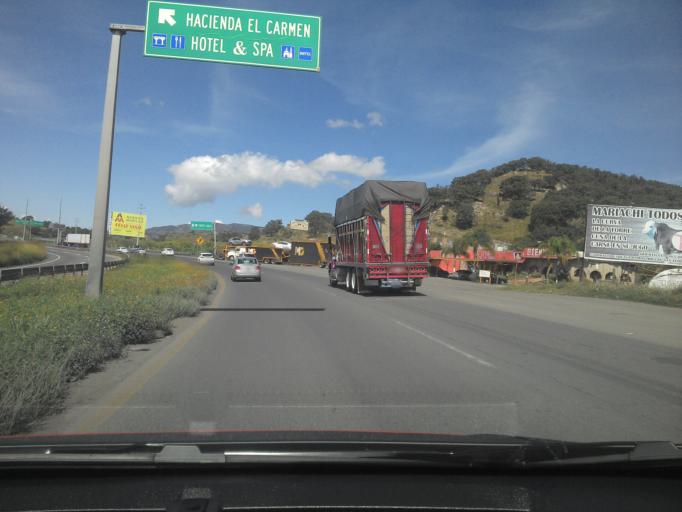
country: MX
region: Jalisco
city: La Venta del Astillero
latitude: 20.7349
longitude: -103.5781
